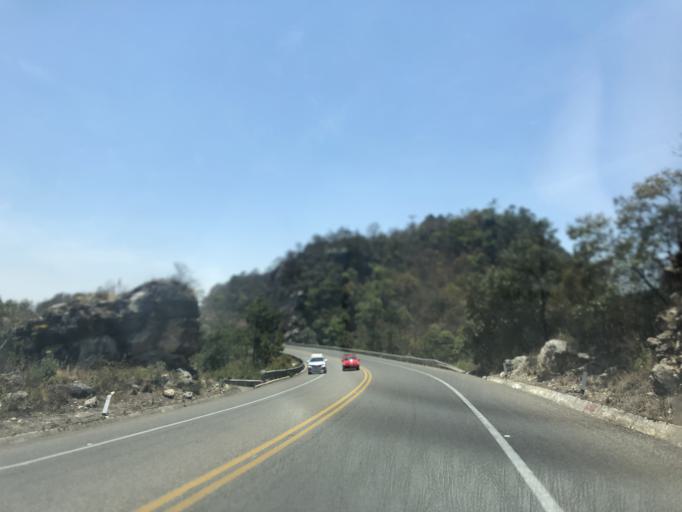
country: MX
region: Chiapas
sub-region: Zinacantan
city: Bochojbo Alto
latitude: 16.7096
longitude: -92.6884
